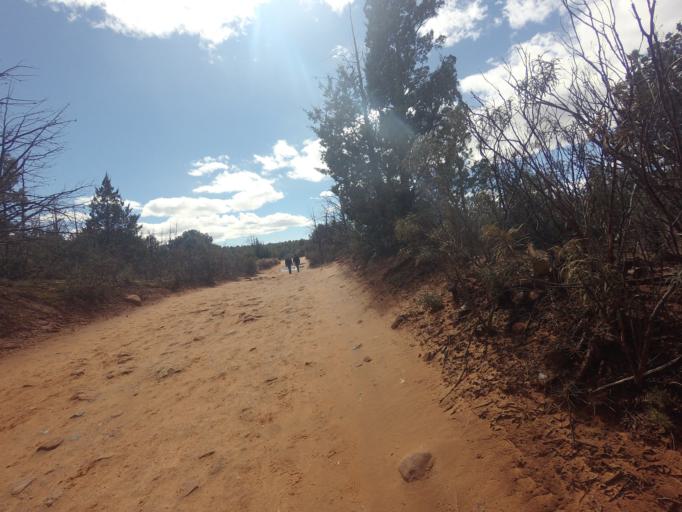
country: US
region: Arizona
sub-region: Yavapai County
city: West Sedona
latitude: 34.8993
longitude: -111.8183
